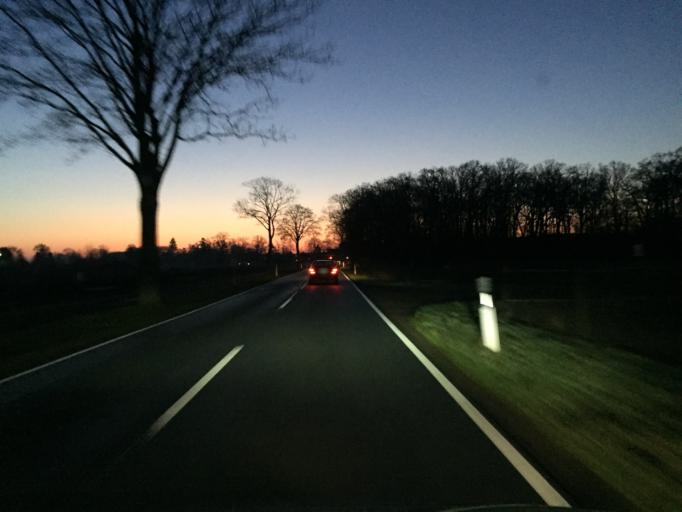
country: DE
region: Lower Saxony
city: Borstel
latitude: 52.6014
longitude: 8.9430
